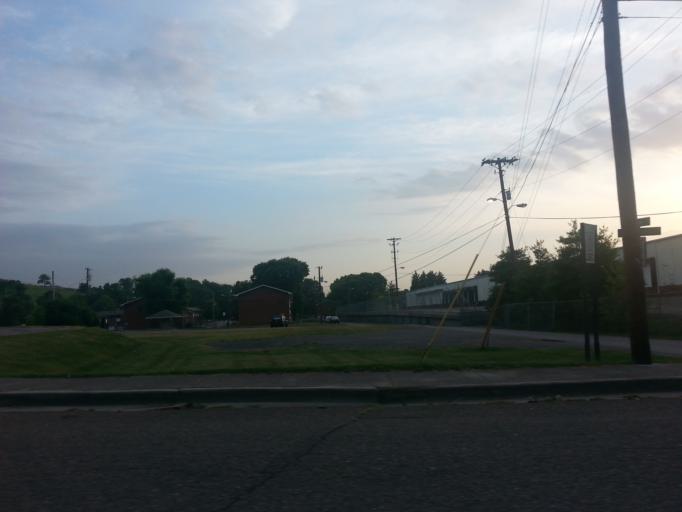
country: US
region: Tennessee
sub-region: Knox County
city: Knoxville
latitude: 35.9731
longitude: -83.9071
